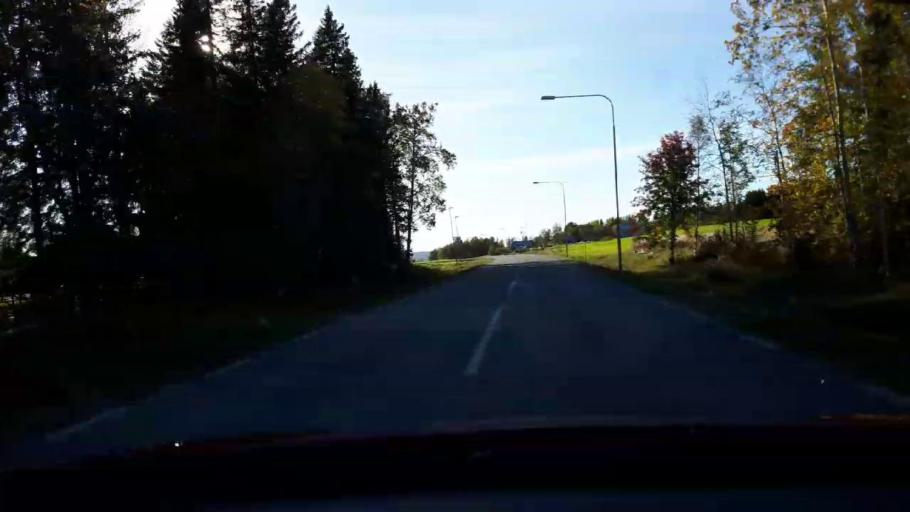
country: SE
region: Jaemtland
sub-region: Stroemsunds Kommun
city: Stroemsund
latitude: 63.8584
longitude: 15.0197
